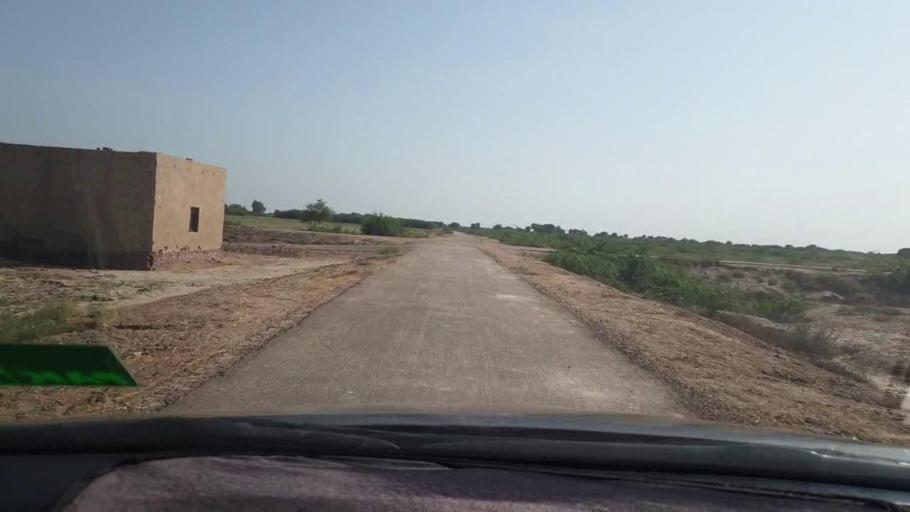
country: PK
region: Sindh
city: Naukot
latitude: 24.9304
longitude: 69.2399
